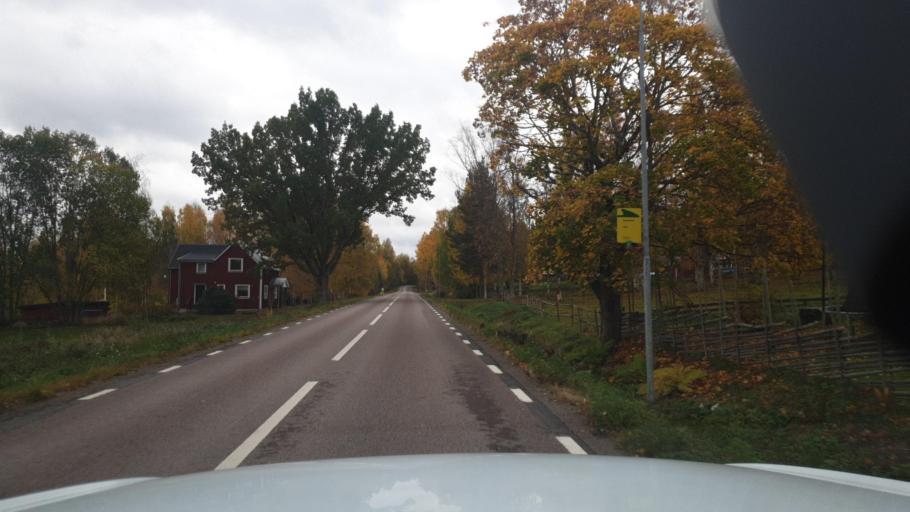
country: SE
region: Vaermland
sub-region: Sunne Kommun
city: Sunne
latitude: 59.8887
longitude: 12.9213
